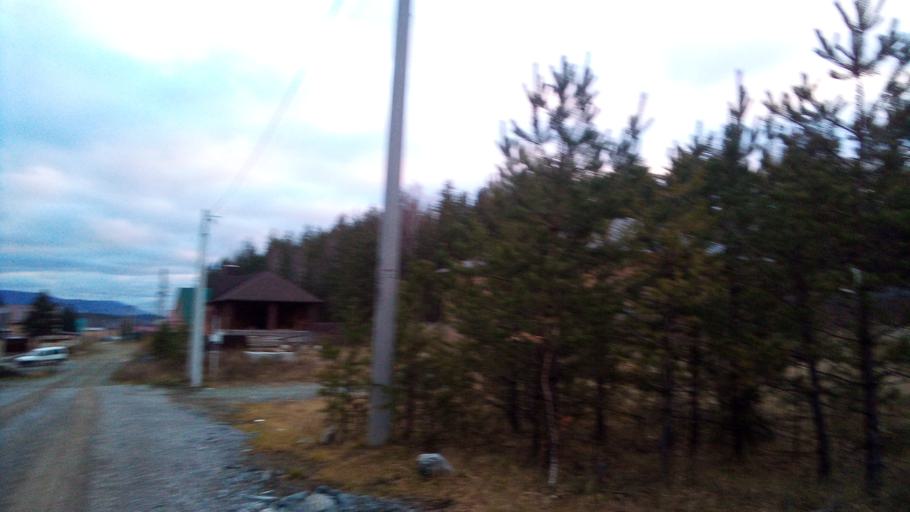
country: RU
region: Chelyabinsk
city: Turgoyak
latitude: 55.1779
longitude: 60.1311
